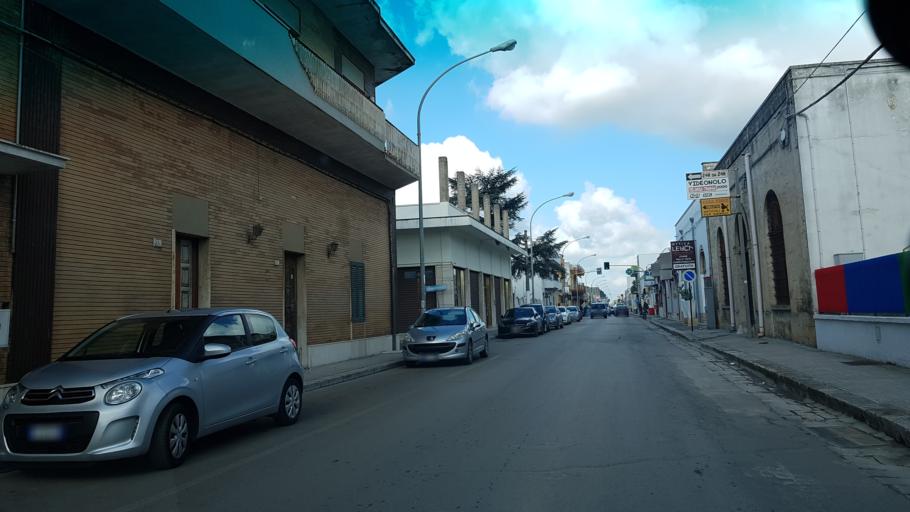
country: IT
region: Apulia
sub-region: Provincia di Lecce
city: Squinzano
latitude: 40.4344
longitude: 18.0411
